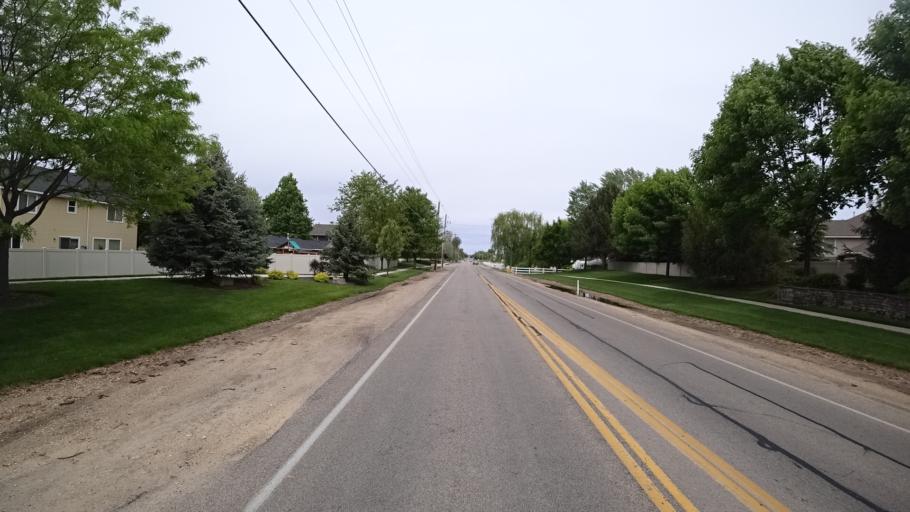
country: US
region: Idaho
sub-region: Ada County
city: Meridian
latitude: 43.5716
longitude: -116.3746
